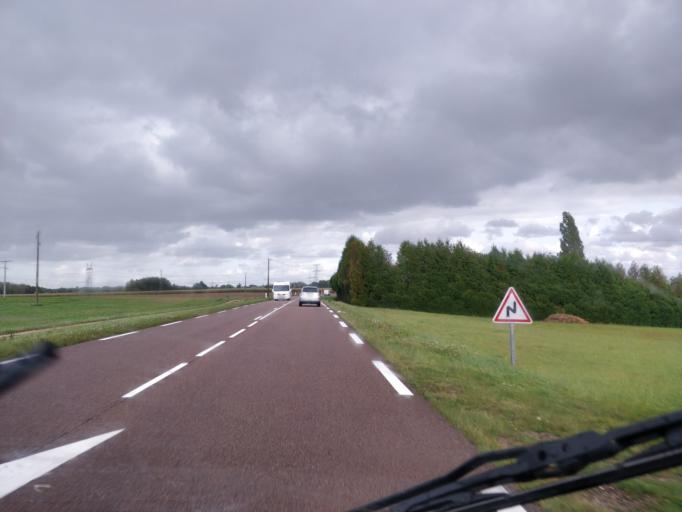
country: FR
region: Champagne-Ardenne
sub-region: Departement de l'Aube
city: Verrieres
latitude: 48.2800
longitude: 4.1923
